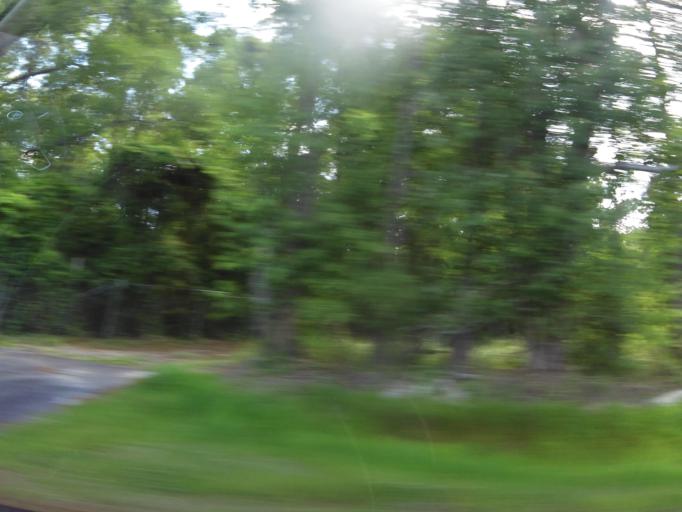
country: US
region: Florida
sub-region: Nassau County
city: Callahan
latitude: 30.6048
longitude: -81.8701
